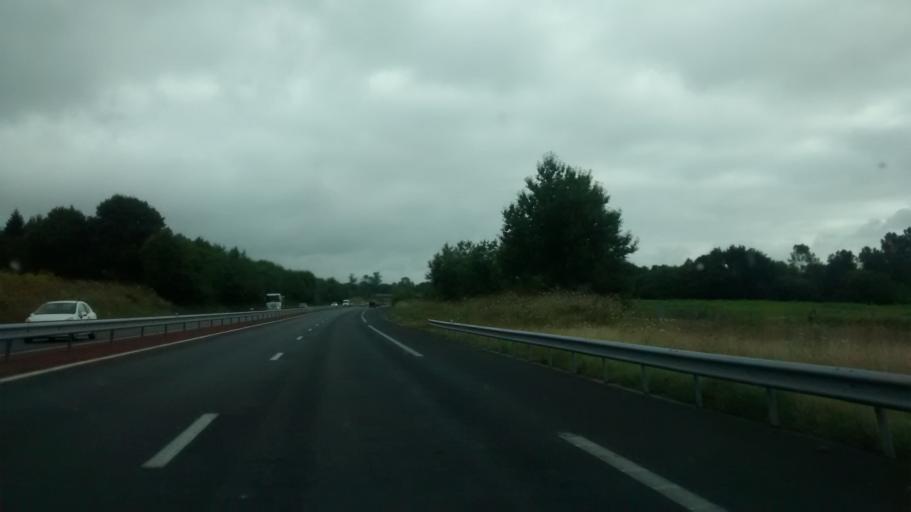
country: FR
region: Lower Normandy
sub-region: Departement de la Manche
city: Villedieu-les-Poeles
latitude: 48.7699
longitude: -1.2768
